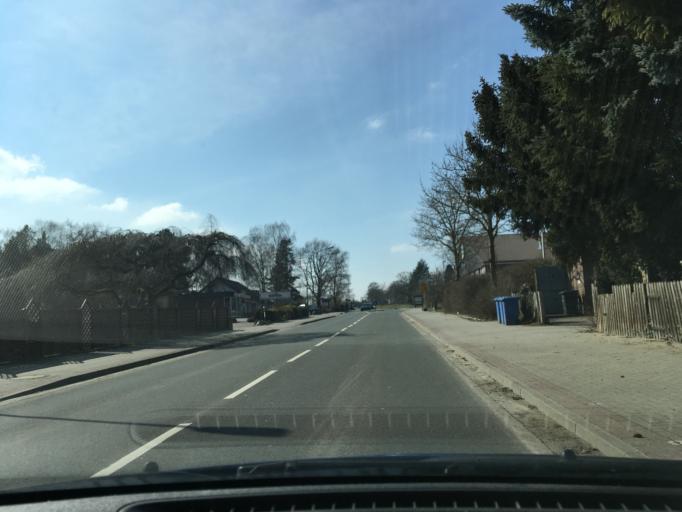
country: DE
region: Lower Saxony
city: Salzhausen
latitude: 53.2266
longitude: 10.1621
